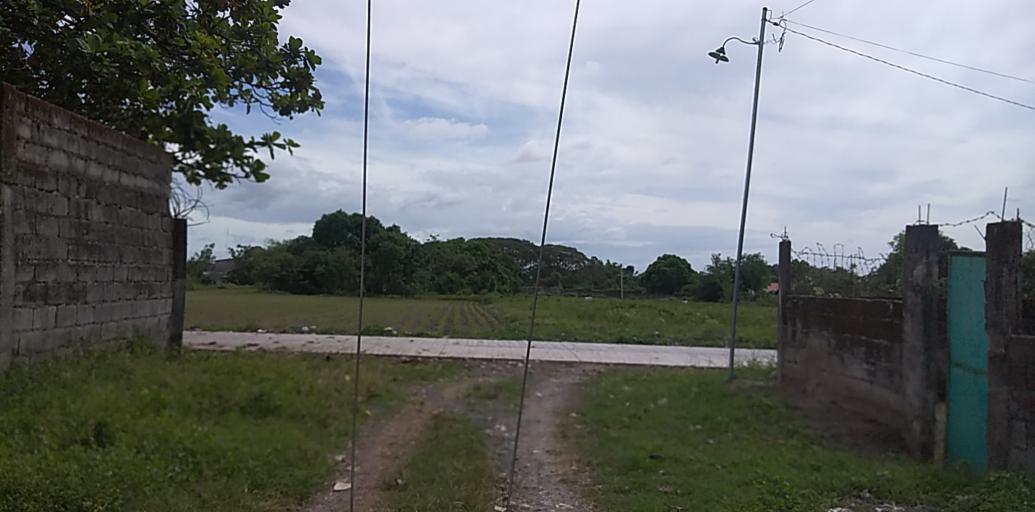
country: PH
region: Central Luzon
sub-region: Province of Pampanga
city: Manibaug Pasig
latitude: 15.1109
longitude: 120.5578
